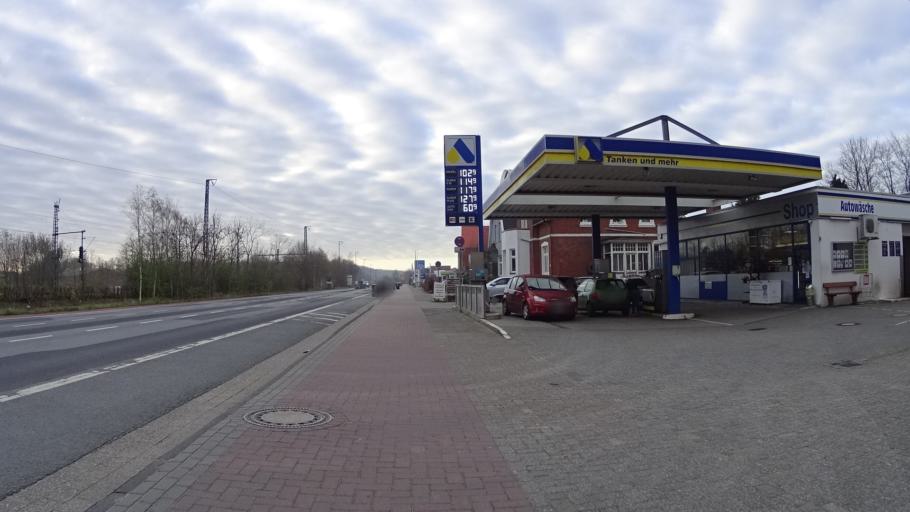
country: DE
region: Lower Saxony
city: Norden
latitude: 53.5859
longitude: 7.2216
